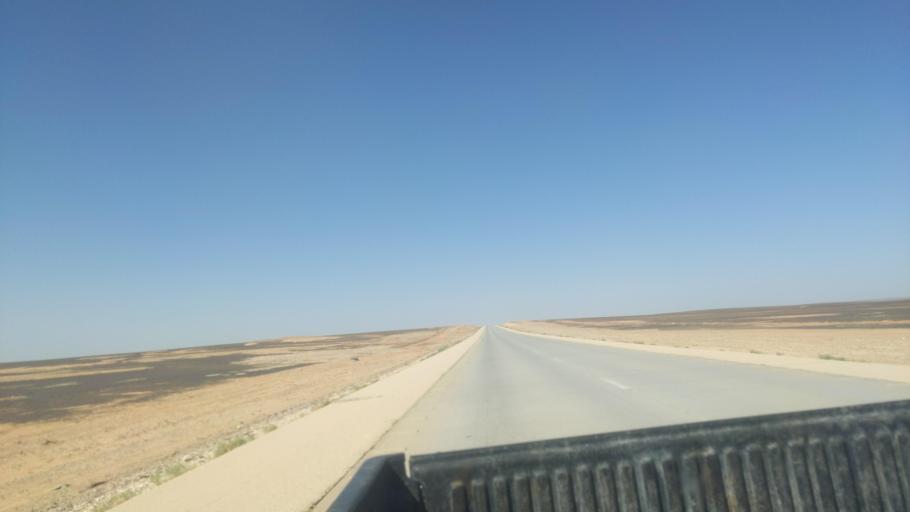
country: JO
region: Amman
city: Al Azraq ash Shamali
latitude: 31.4381
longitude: 36.7492
